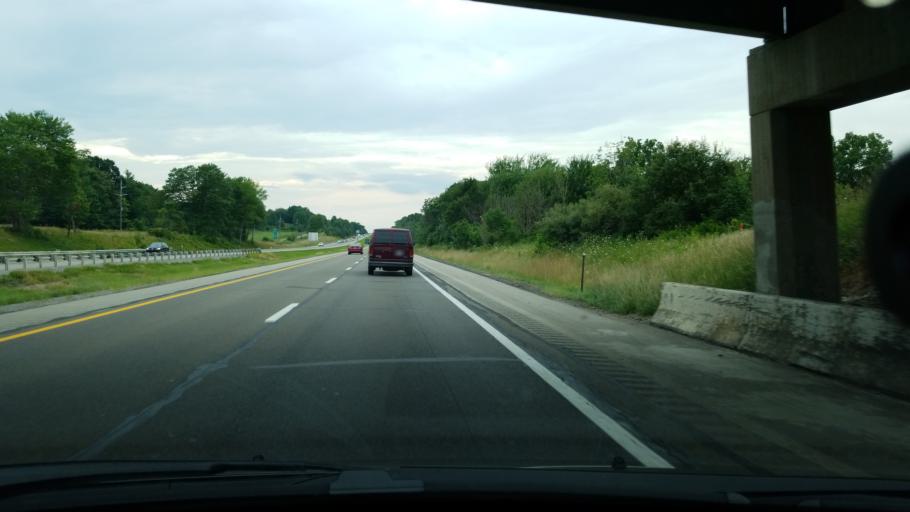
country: US
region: Ohio
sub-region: Mahoning County
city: New Middletown
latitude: 40.9413
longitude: -80.5956
